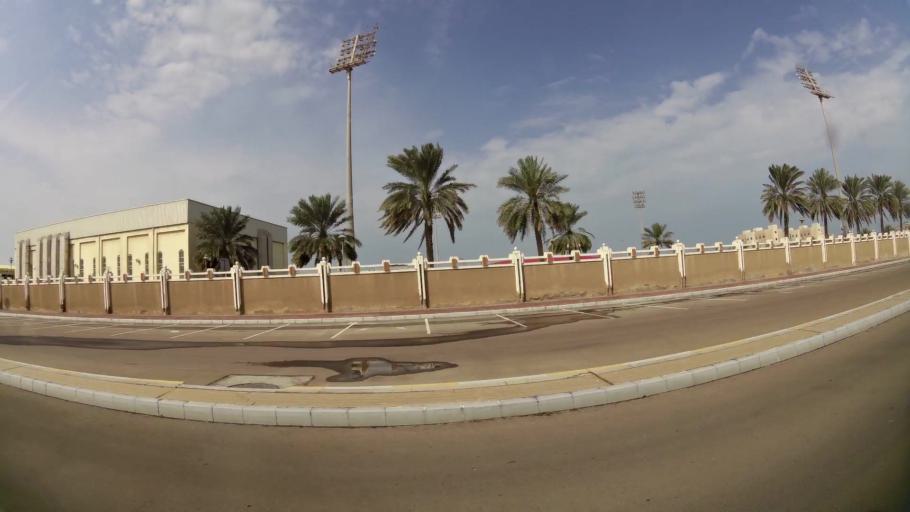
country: AE
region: Abu Dhabi
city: Abu Dhabi
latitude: 24.4373
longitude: 54.4271
